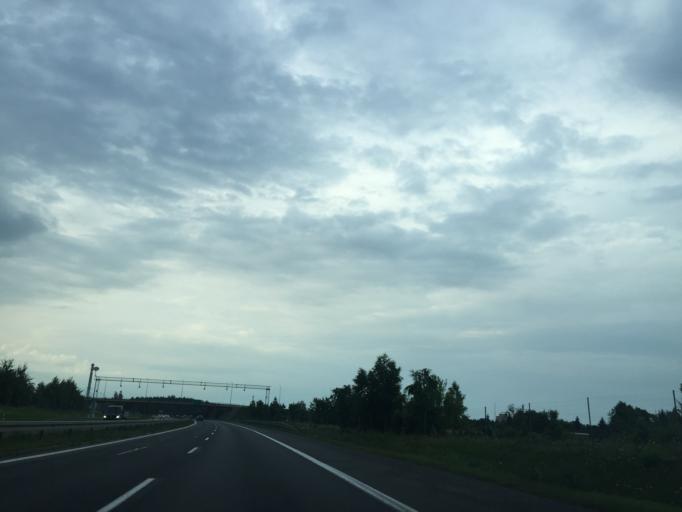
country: PL
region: Masovian Voivodeship
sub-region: Powiat ostrowski
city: Ostrow Mazowiecka
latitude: 52.8077
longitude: 21.8760
